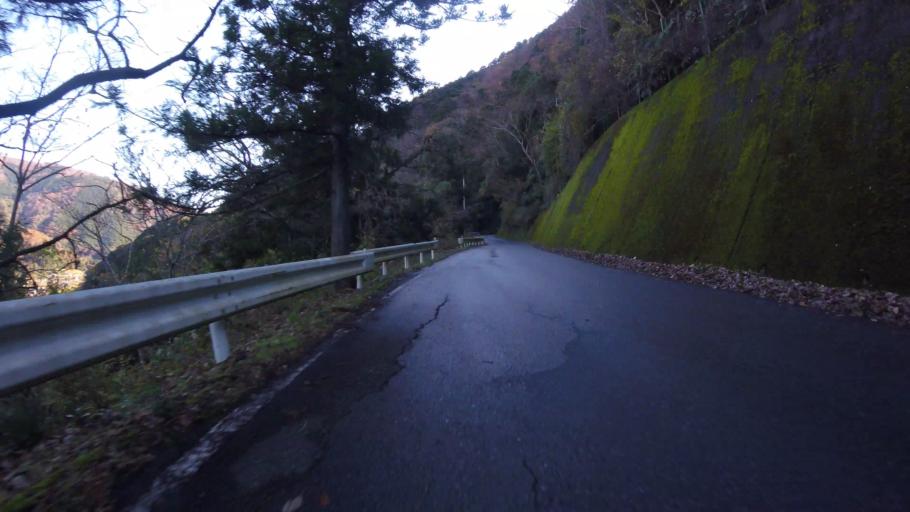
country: JP
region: Shizuoka
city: Shimoda
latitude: 34.7667
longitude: 138.9636
